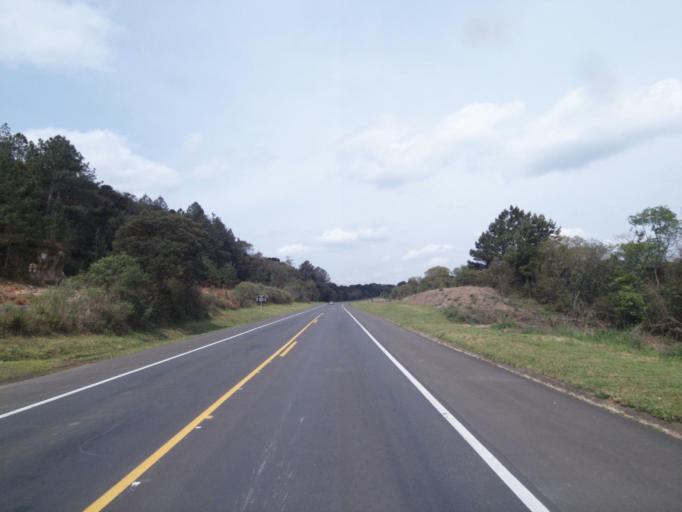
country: BR
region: Parana
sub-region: Irati
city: Irati
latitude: -25.4539
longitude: -50.4436
